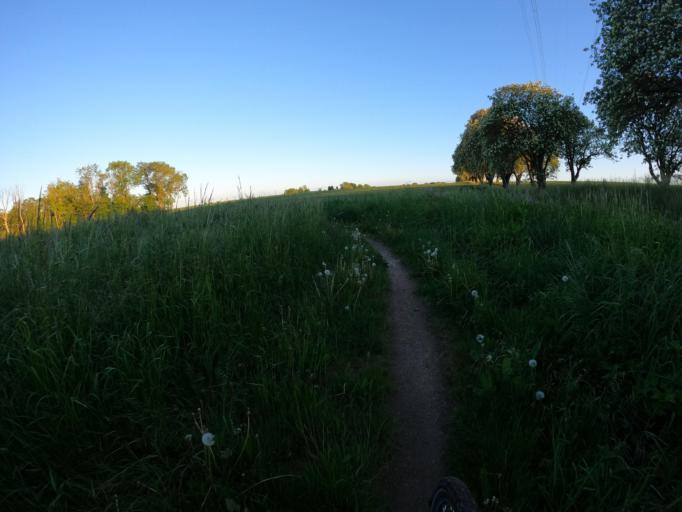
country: DK
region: Capital Region
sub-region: Hoje-Taastrup Kommune
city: Flong
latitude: 55.6271
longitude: 12.2214
